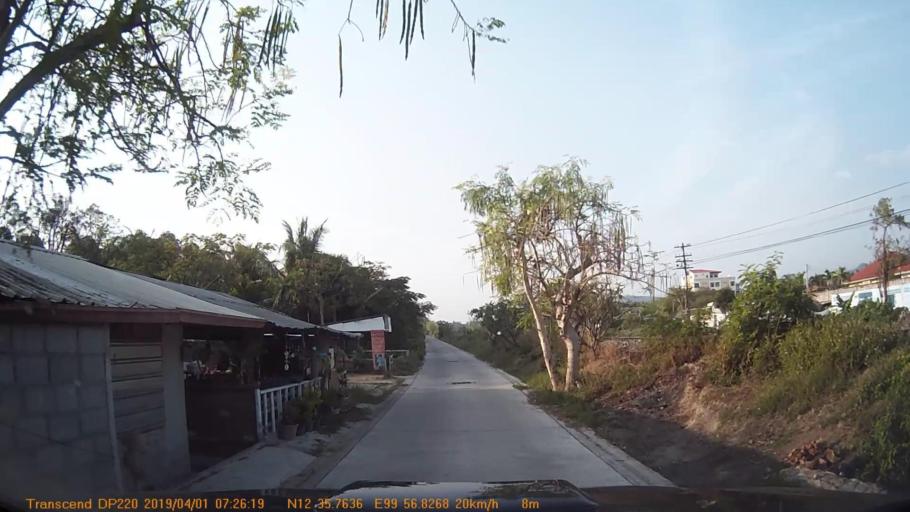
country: TH
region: Prachuap Khiri Khan
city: Hua Hin
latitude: 12.5959
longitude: 99.9471
